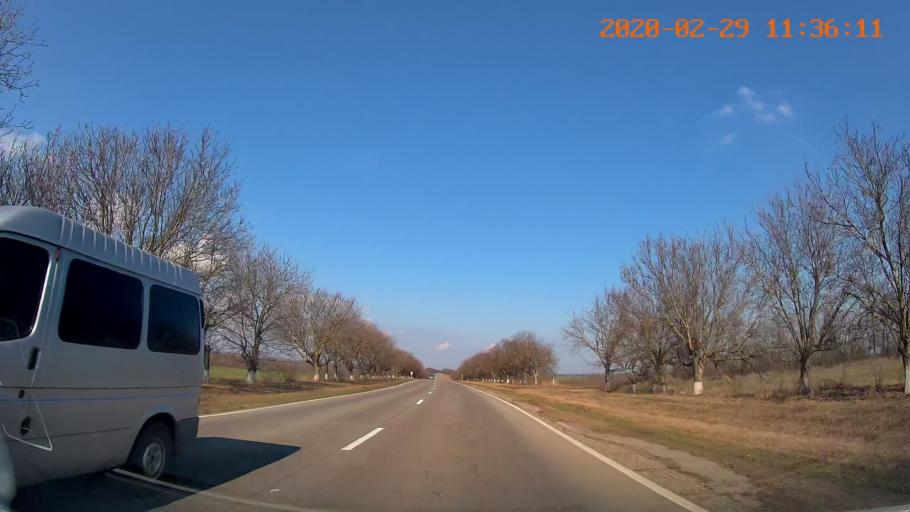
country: MD
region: Rezina
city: Saharna
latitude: 47.5923
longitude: 29.0582
